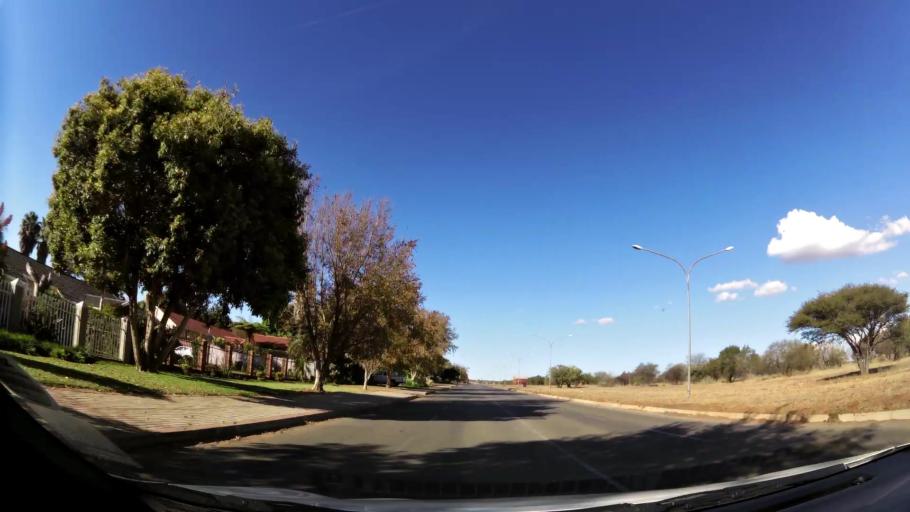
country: ZA
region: Limpopo
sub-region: Capricorn District Municipality
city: Polokwane
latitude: -23.9177
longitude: 29.4867
